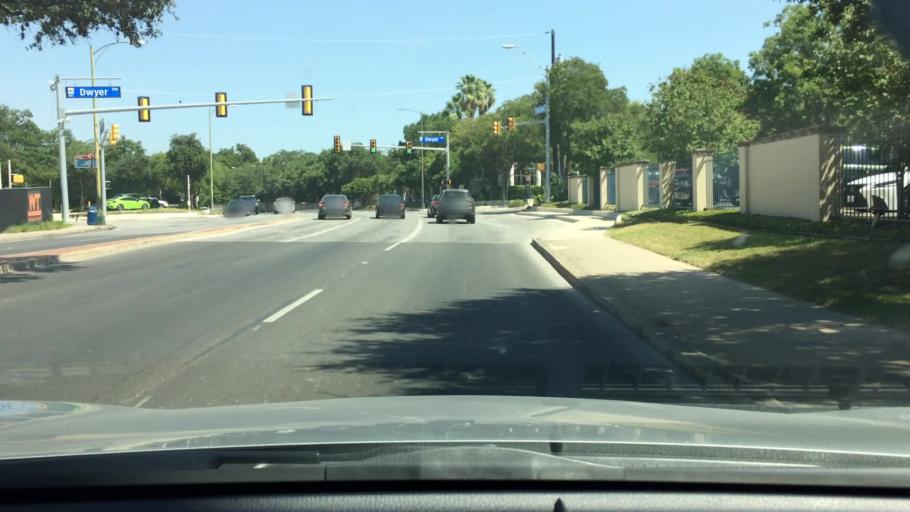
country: US
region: Texas
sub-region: Bexar County
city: San Antonio
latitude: 29.4191
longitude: -98.4949
